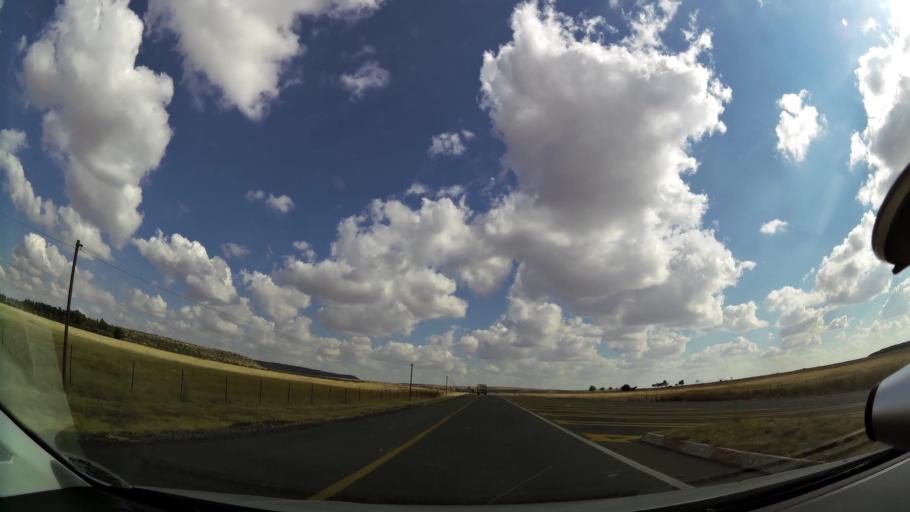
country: ZA
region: Orange Free State
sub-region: Mangaung Metropolitan Municipality
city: Bloemfontein
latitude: -29.1447
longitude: 26.0853
